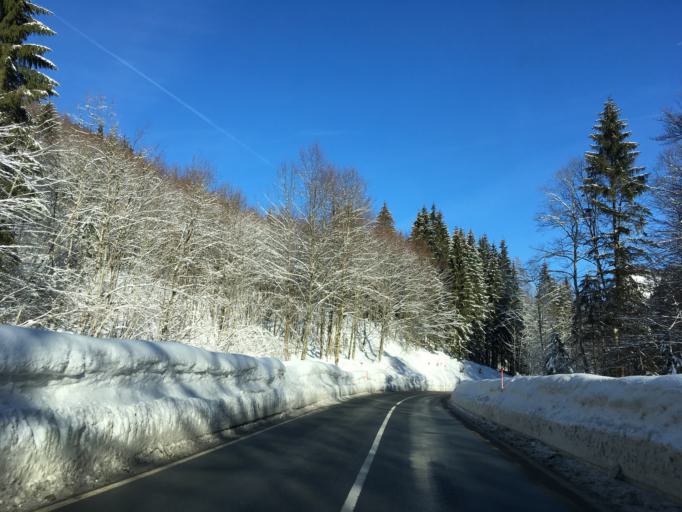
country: DE
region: Bavaria
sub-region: Upper Bavaria
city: Aschau im Chiemgau
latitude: 47.7221
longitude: 12.2925
